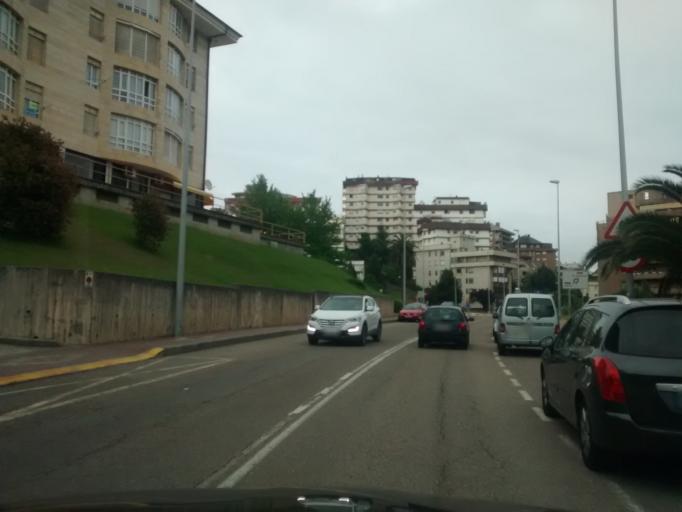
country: ES
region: Cantabria
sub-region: Provincia de Cantabria
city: Santander
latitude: 43.4780
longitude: -3.7948
